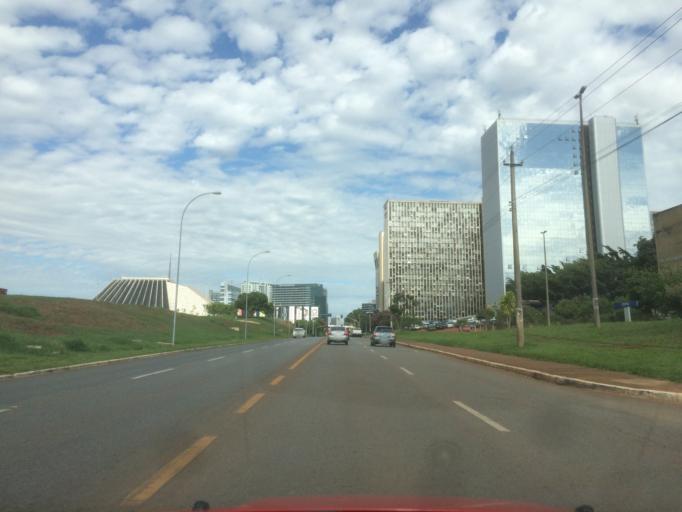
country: BR
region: Federal District
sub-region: Brasilia
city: Brasilia
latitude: -15.7926
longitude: -47.8767
